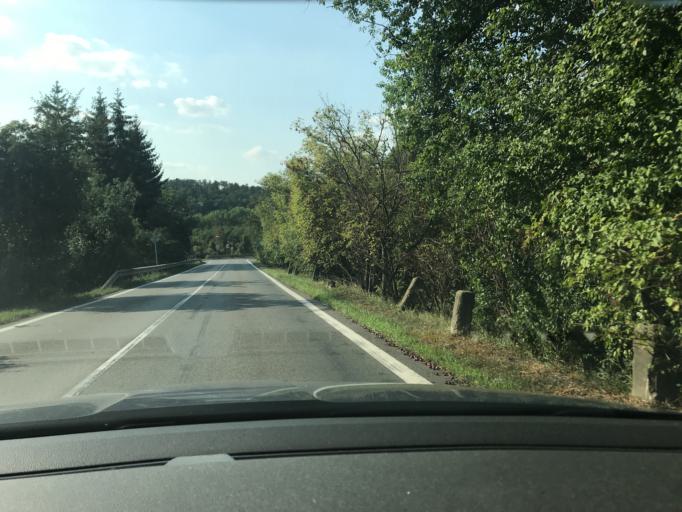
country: CZ
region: Central Bohemia
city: Kralupy nad Vltavou
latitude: 50.2196
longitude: 14.3002
